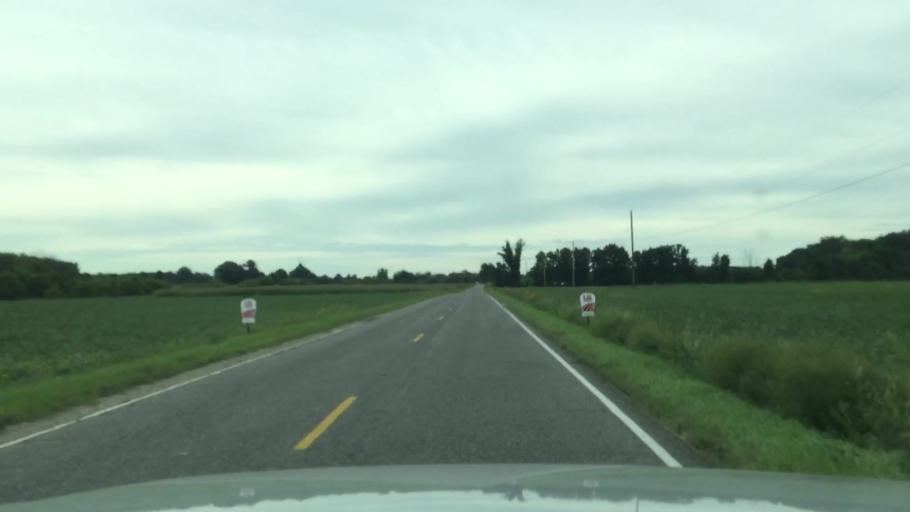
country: US
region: Michigan
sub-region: Genesee County
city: Flushing
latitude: 43.0695
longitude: -83.9876
